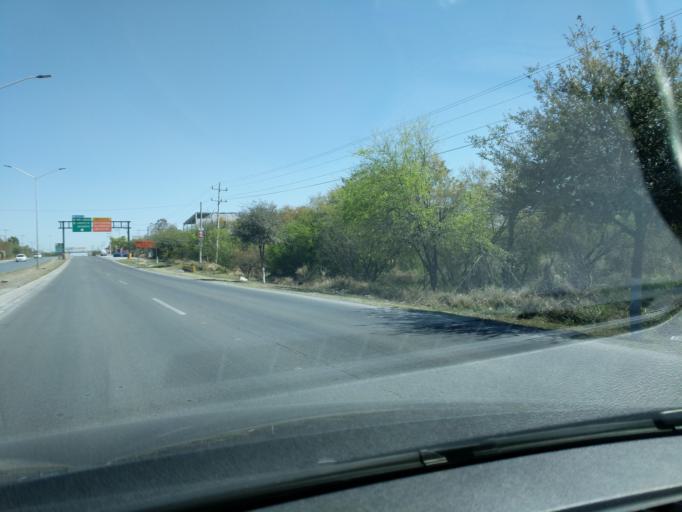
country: MX
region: Nuevo Leon
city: Juarez
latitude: 25.6337
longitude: -100.0794
